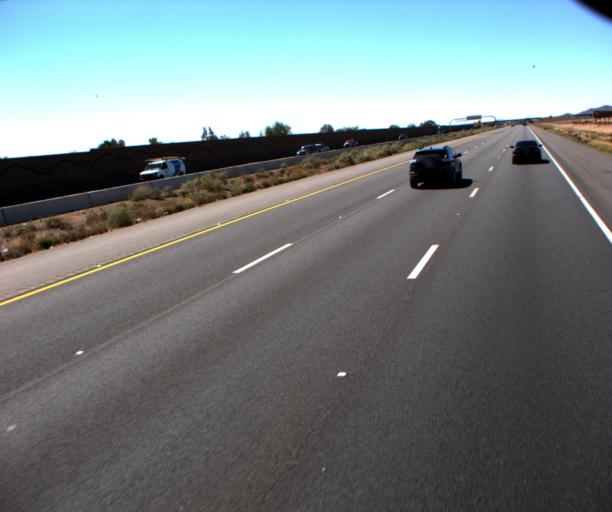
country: US
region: Arizona
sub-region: Pinal County
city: Casa Grande
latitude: 32.8734
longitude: -111.6872
